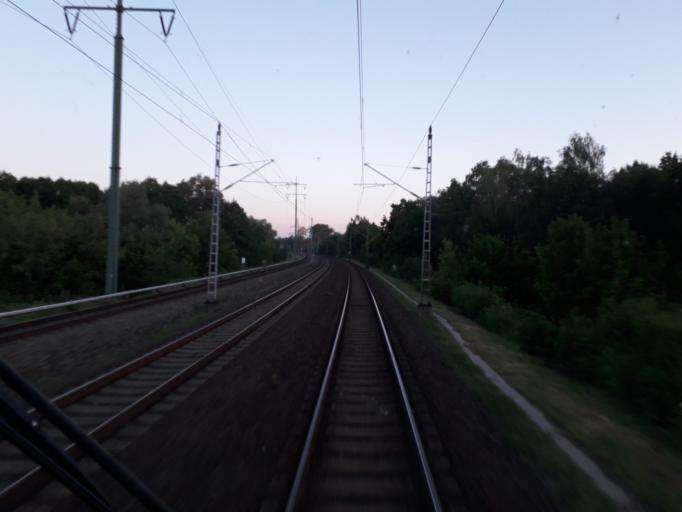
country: DE
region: Berlin
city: Blankenfelde
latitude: 52.6520
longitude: 13.3936
